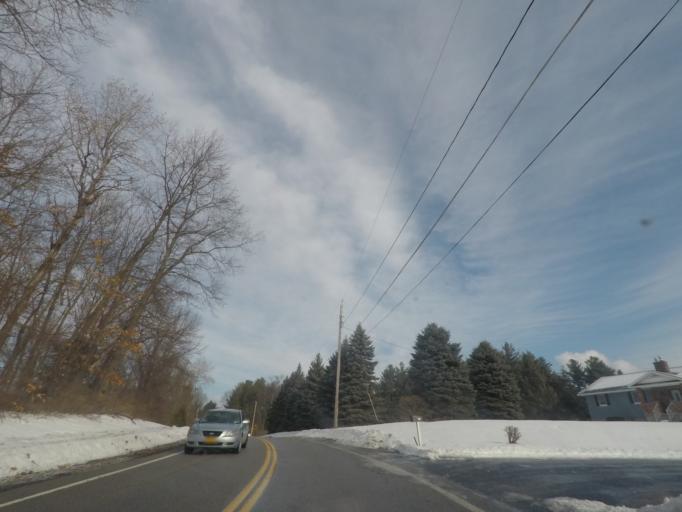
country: US
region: New York
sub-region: Saratoga County
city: Country Knolls
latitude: 42.8754
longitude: -73.7514
